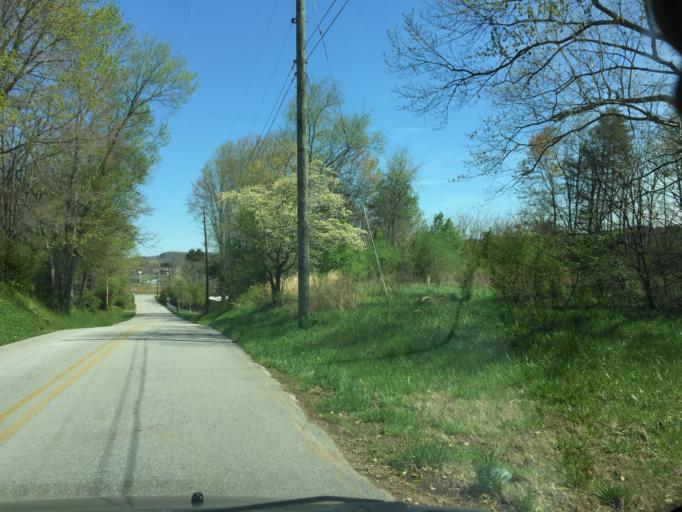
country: US
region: Tennessee
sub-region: Hamilton County
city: Soddy-Daisy
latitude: 35.2347
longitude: -85.2042
